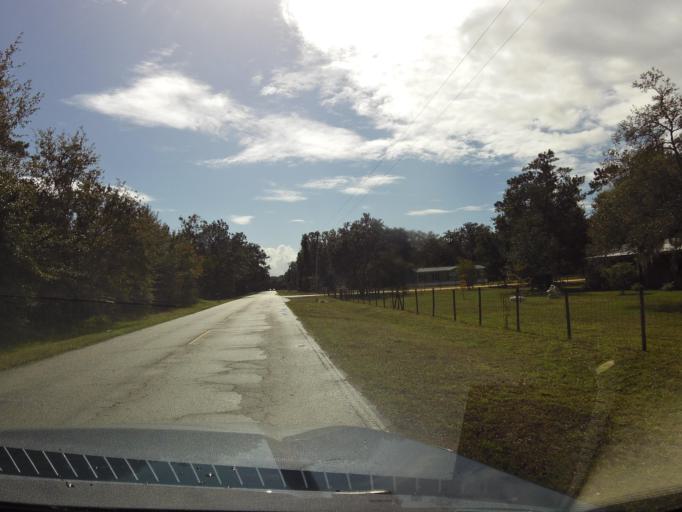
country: US
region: Florida
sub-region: Clay County
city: Asbury Lake
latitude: 29.9870
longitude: -81.8396
